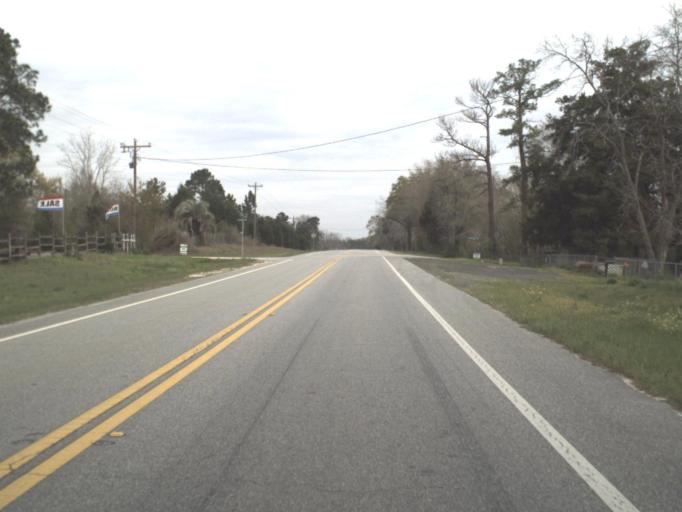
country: US
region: Florida
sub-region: Jackson County
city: Graceville
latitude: 30.9428
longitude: -85.6490
